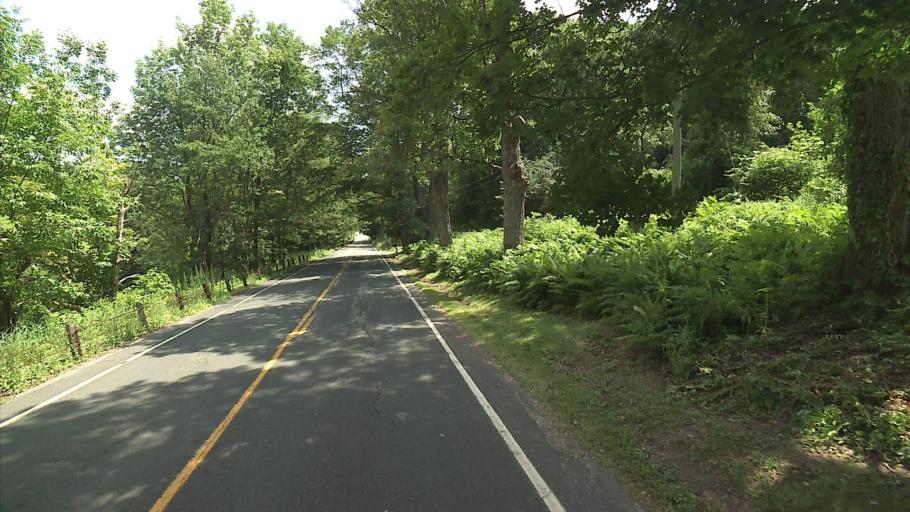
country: US
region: Connecticut
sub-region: Litchfield County
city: Winsted
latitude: 41.9807
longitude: -73.1072
